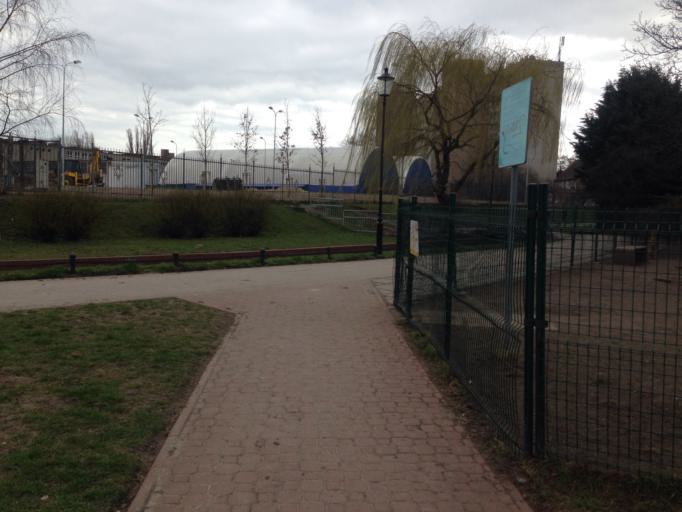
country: PL
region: Pomeranian Voivodeship
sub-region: Gdansk
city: Gdansk
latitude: 54.3802
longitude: 18.6194
